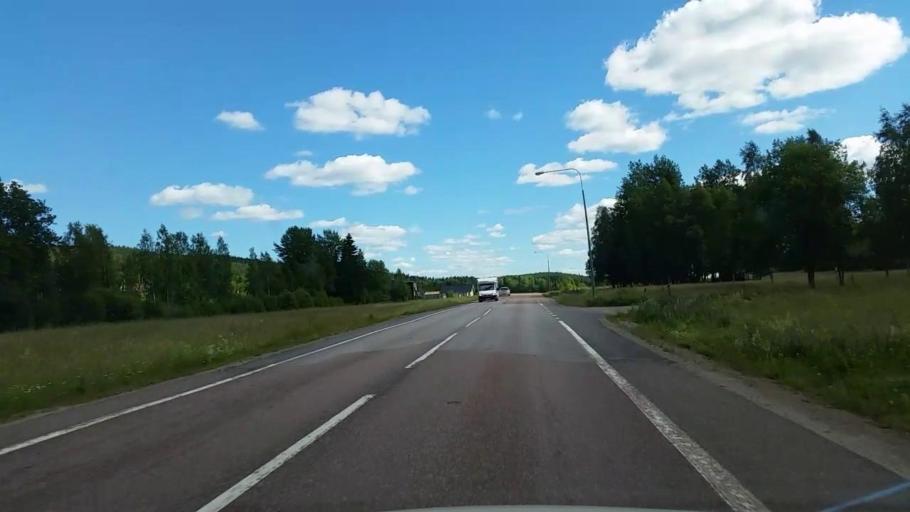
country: SE
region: Dalarna
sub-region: Faluns Kommun
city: Svardsjo
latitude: 60.8487
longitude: 15.7556
